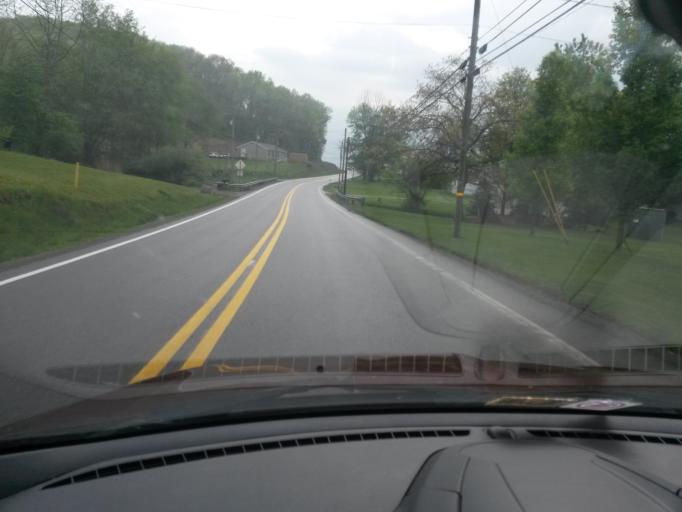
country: US
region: West Virginia
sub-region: Randolph County
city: Elkins
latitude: 38.7727
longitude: -79.9239
